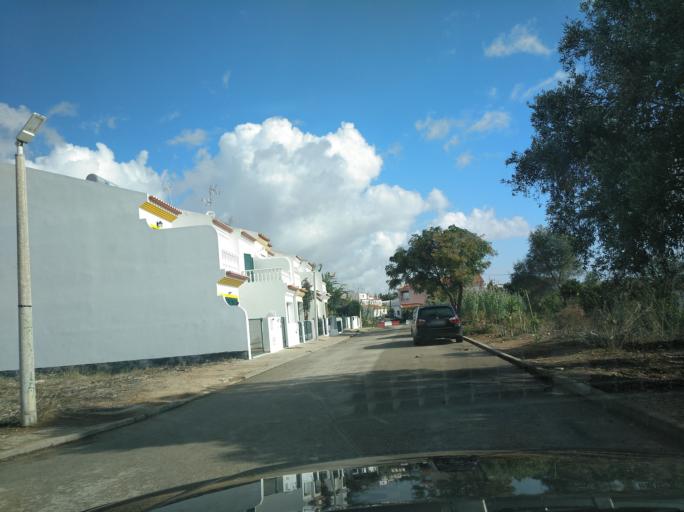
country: PT
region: Faro
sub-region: Vila Real de Santo Antonio
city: Monte Gordo
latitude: 37.1792
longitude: -7.4992
